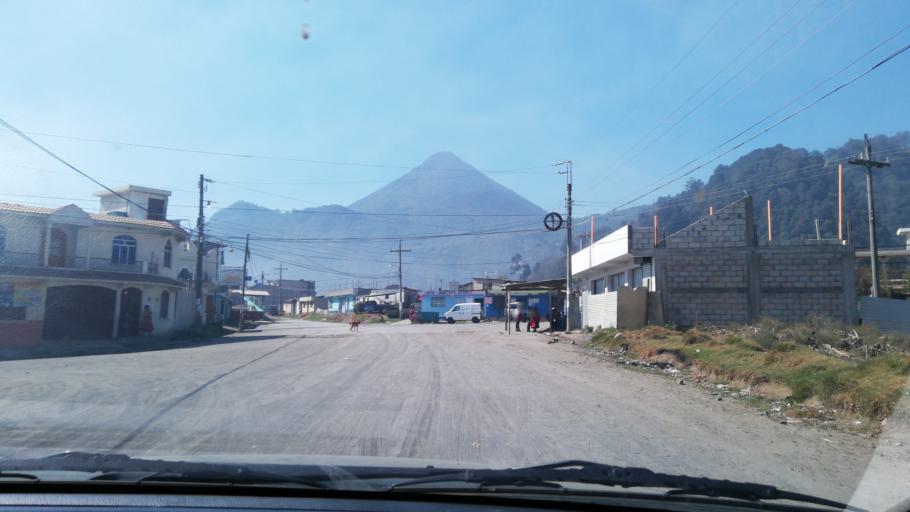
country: GT
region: Quetzaltenango
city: Quetzaltenango
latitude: 14.8036
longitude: -91.5515
